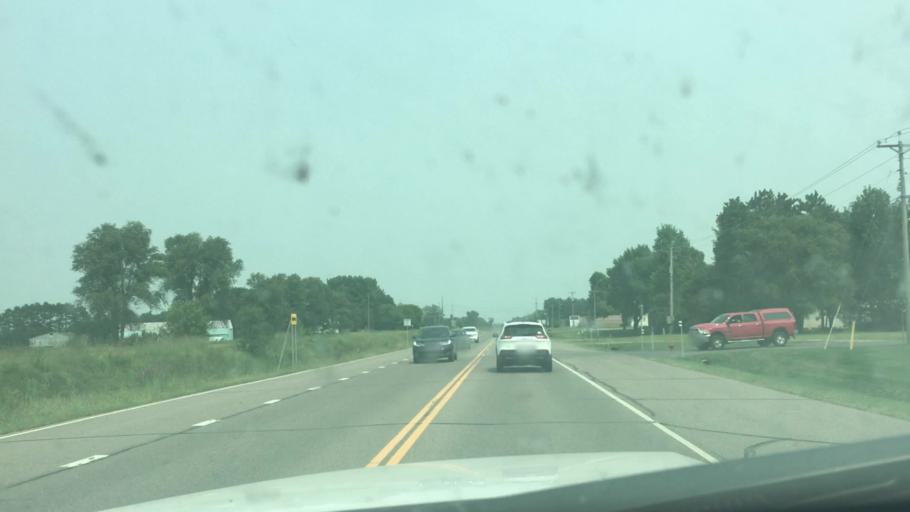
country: US
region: Minnesota
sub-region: Washington County
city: Hugo
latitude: 45.1678
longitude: -92.9910
